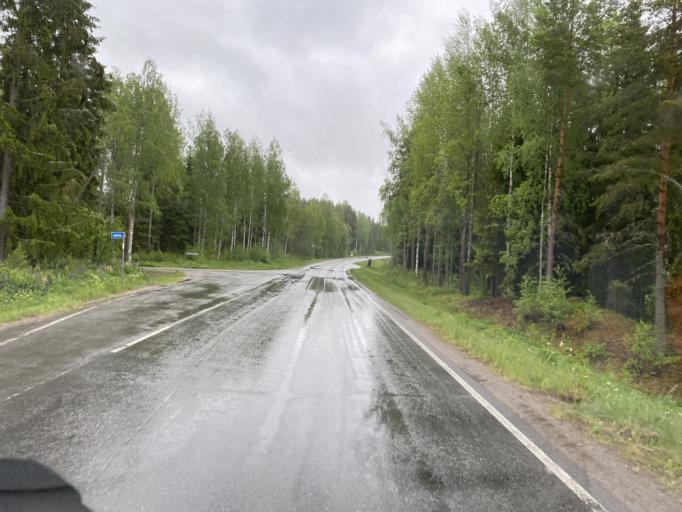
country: FI
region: Pirkanmaa
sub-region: Etelae-Pirkanmaa
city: Urjala
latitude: 61.0405
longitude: 23.4420
